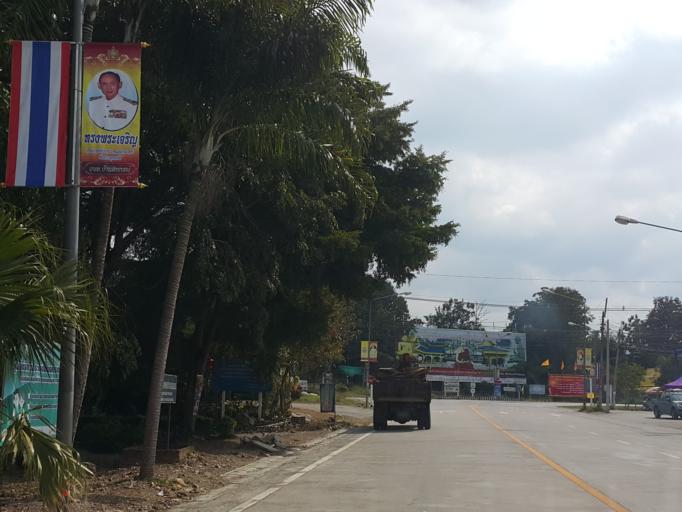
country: TH
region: Chiang Mai
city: Mae On
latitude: 18.7978
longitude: 99.2438
